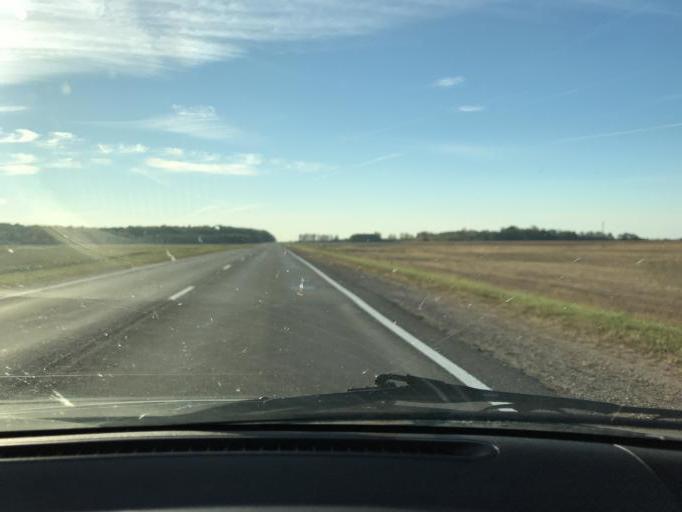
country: BY
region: Brest
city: Antopal'
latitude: 52.2270
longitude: 24.7781
